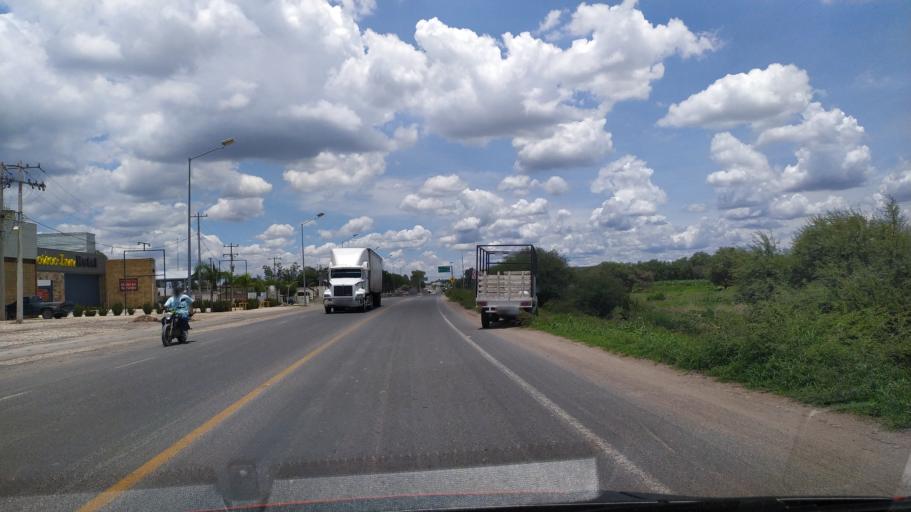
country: MX
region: Guanajuato
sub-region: San Francisco del Rincon
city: Fraccionamiento Villa Jardin
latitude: 20.9970
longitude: -101.8560
